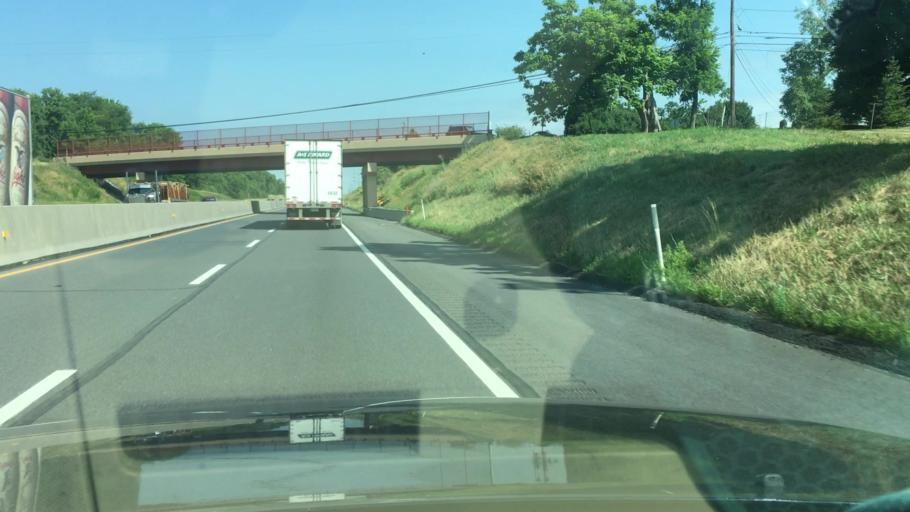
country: US
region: Pennsylvania
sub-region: Lehigh County
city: Wescosville
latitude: 40.5540
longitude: -75.5407
